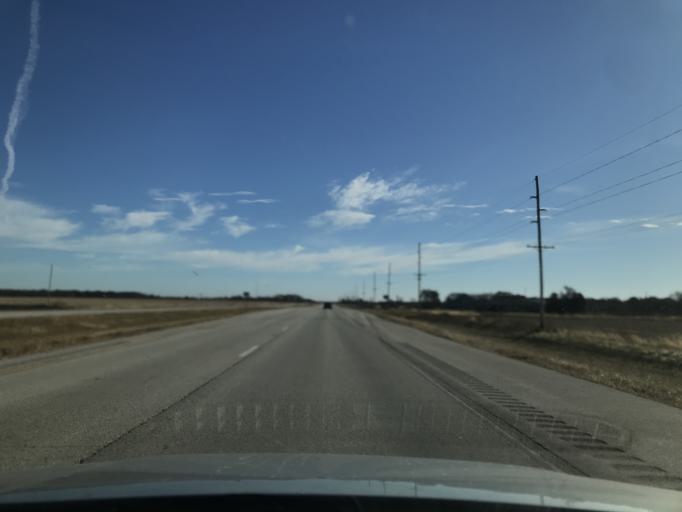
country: US
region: Illinois
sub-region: Hancock County
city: Carthage
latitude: 40.4151
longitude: -91.0557
